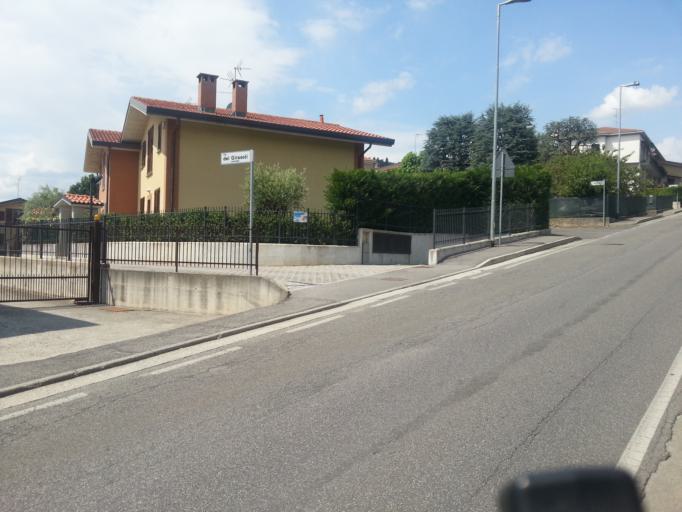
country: IT
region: Lombardy
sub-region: Provincia di Lecco
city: Quattro Strade
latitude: 45.6975
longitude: 9.3775
